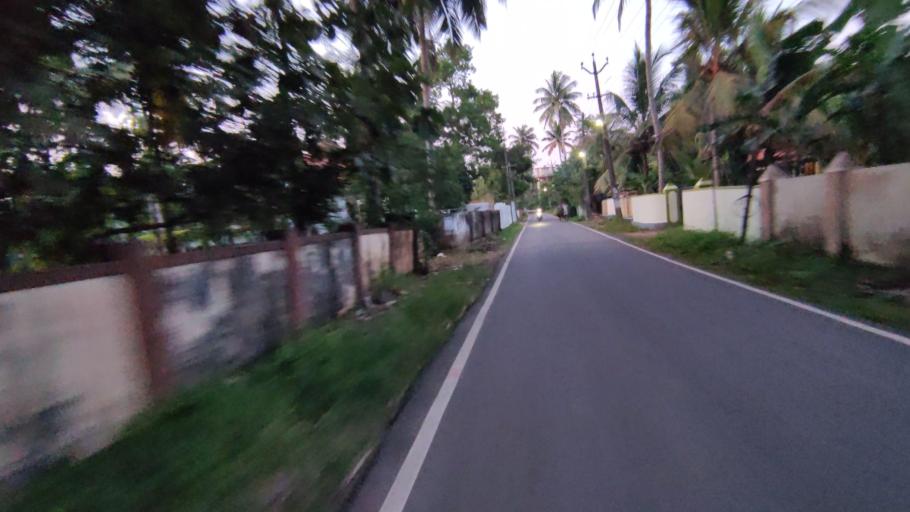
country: IN
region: Kerala
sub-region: Kottayam
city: Kottayam
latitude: 9.5790
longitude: 76.4353
